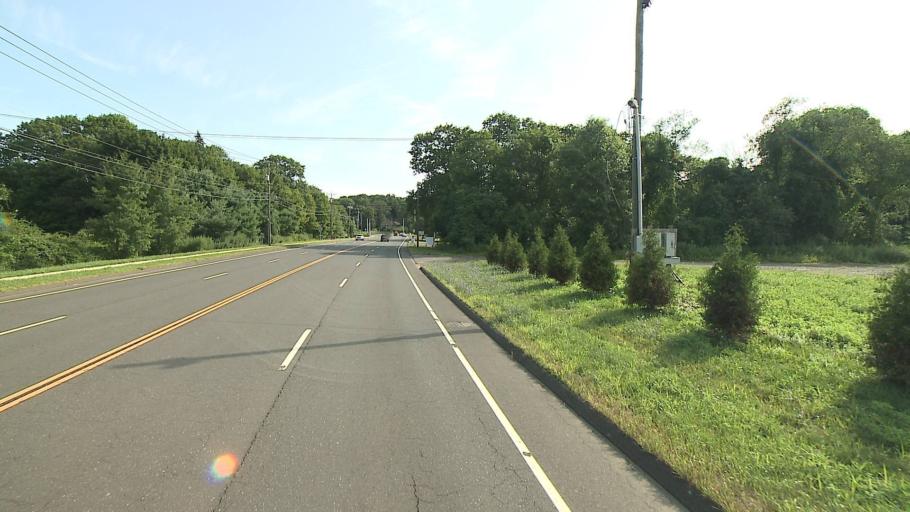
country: US
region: Connecticut
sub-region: Fairfield County
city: Wilton
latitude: 41.2152
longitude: -73.4305
